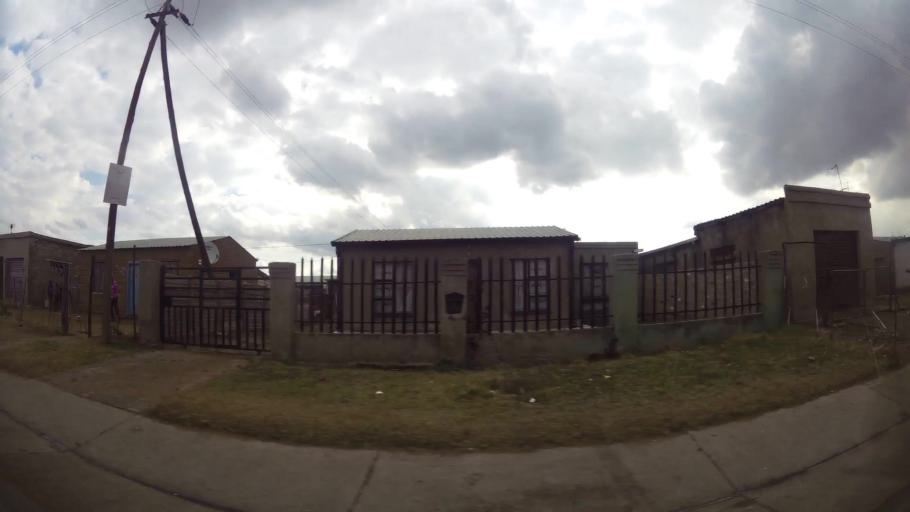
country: ZA
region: Orange Free State
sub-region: Fezile Dabi District Municipality
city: Sasolburg
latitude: -26.8548
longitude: 27.8592
